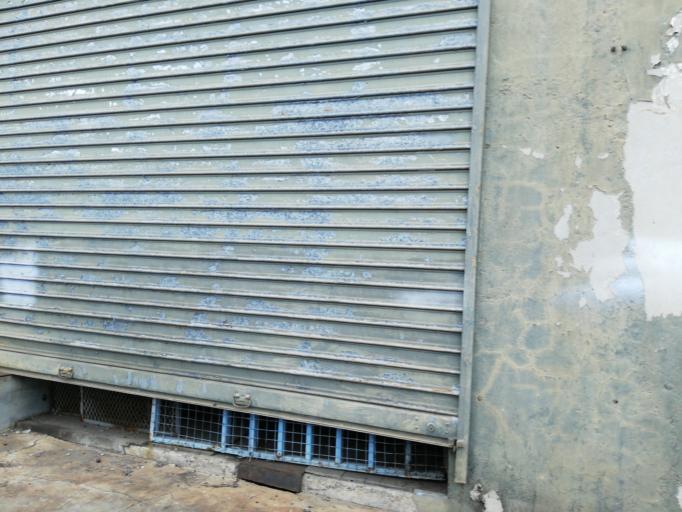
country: MU
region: Black River
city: Petite Riviere
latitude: -20.1887
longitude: 57.4659
